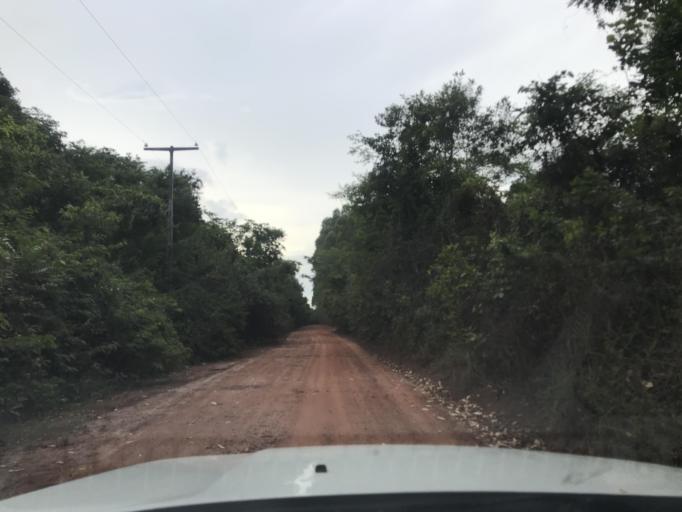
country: BR
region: Bahia
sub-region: Entre Rios
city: Entre Rios
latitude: -12.1135
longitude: -38.1808
